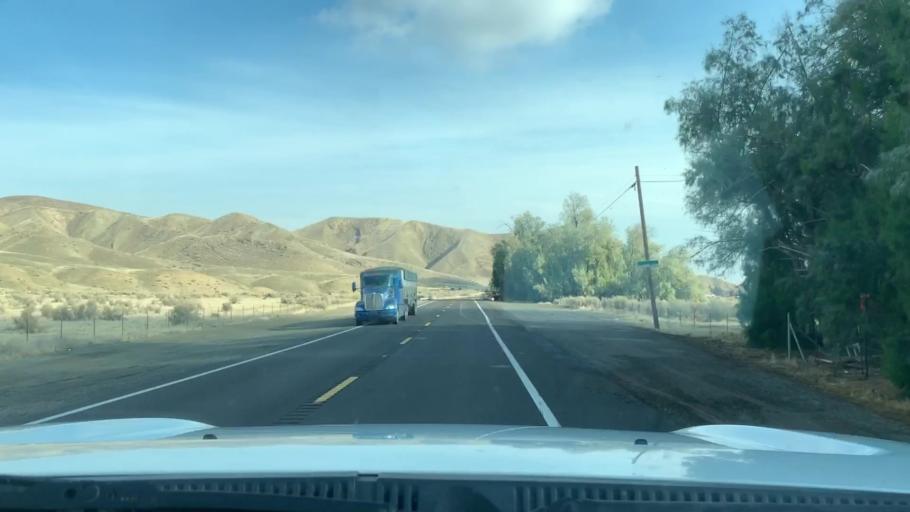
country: US
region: California
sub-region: Fresno County
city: Coalinga
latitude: 36.1052
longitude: -120.4037
